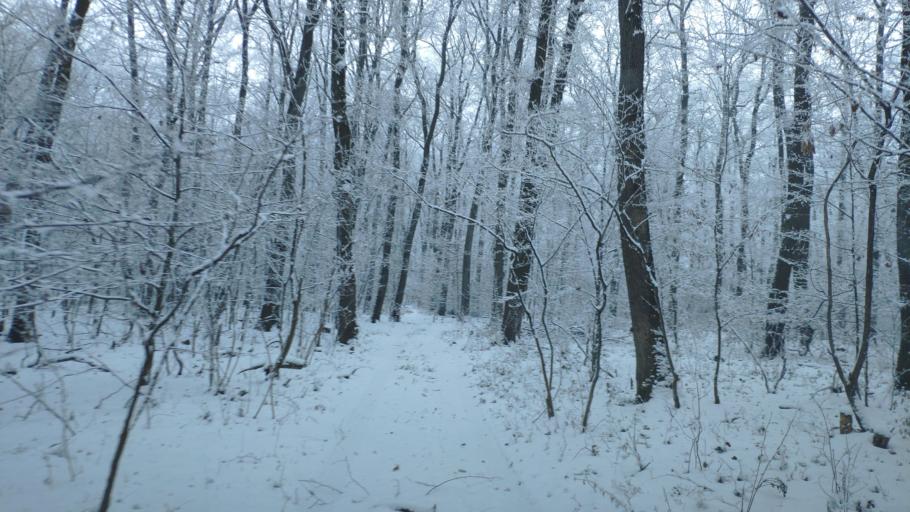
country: SK
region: Kosicky
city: Kosice
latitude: 48.6496
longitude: 21.1824
